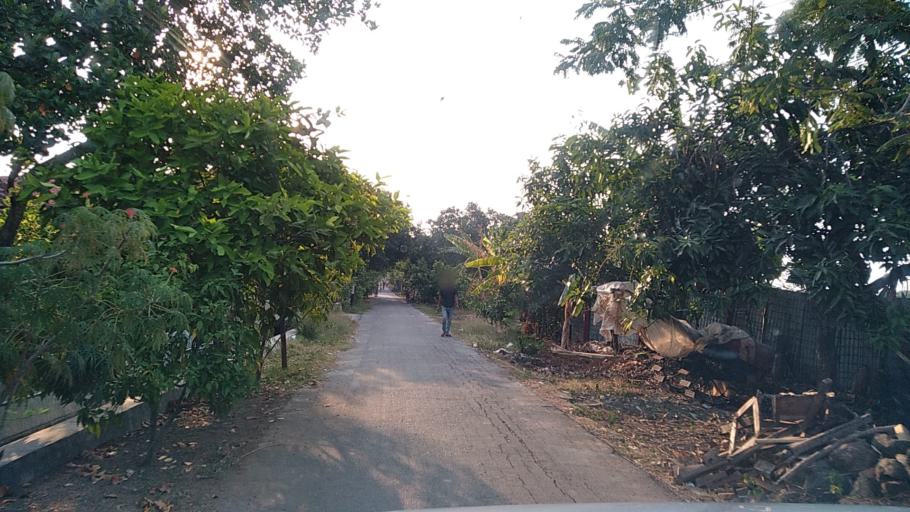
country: ID
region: Central Java
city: Semarang
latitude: -6.9688
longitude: 110.2983
